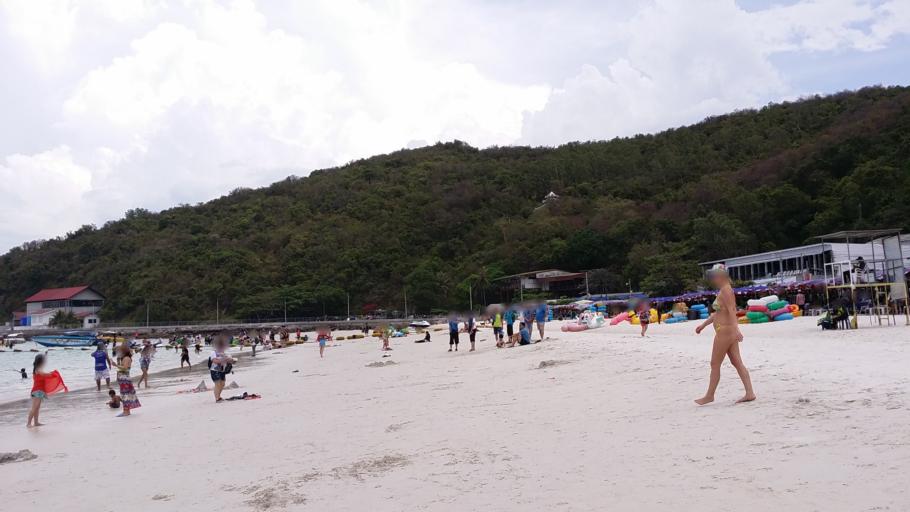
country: TH
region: Chon Buri
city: Ban Ko Lan
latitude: 12.9255
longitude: 100.7794
